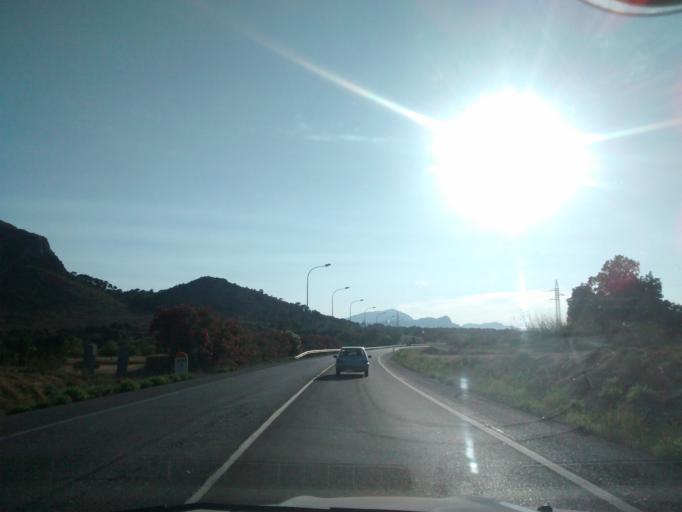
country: ES
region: Balearic Islands
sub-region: Illes Balears
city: Alcudia
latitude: 39.8419
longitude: 3.1050
